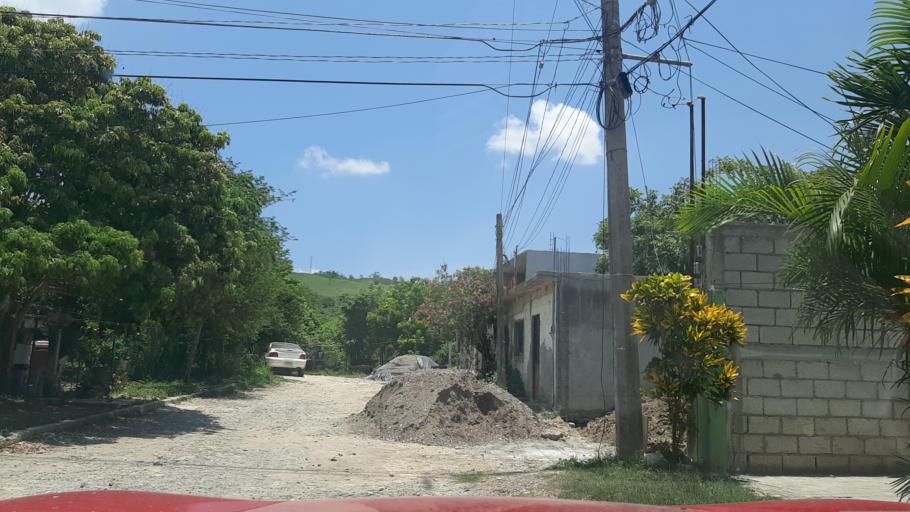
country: MX
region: Veracruz
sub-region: Poza Rica de Hidalgo
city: El Mollejon
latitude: 20.5410
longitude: -97.4093
